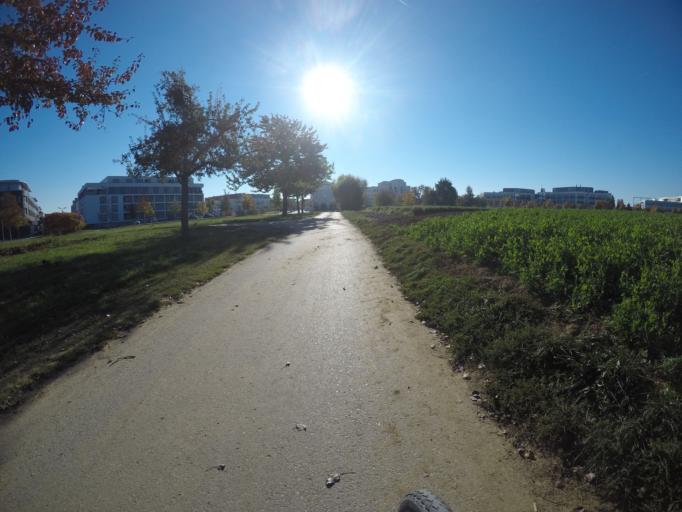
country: DE
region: Baden-Wuerttemberg
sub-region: Regierungsbezirk Stuttgart
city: Leinfelden-Echterdingen
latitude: 48.6941
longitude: 9.1594
